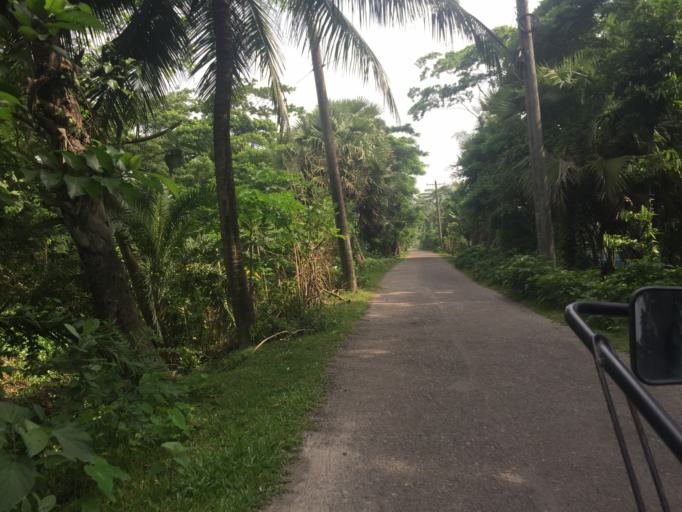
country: BD
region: Barisal
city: Mathba
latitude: 22.2242
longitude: 89.9162
